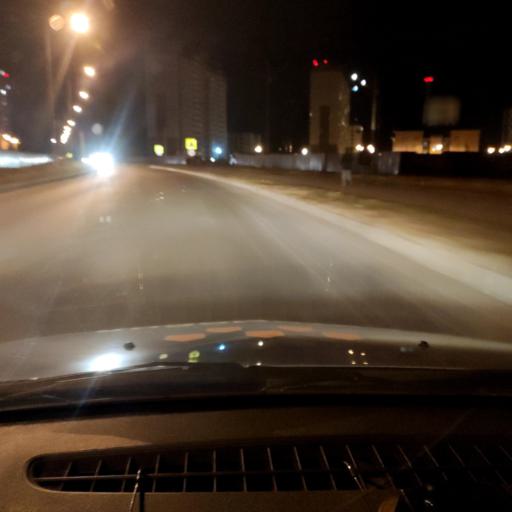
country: RU
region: Voronezj
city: Shilovo
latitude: 51.5695
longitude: 39.1214
